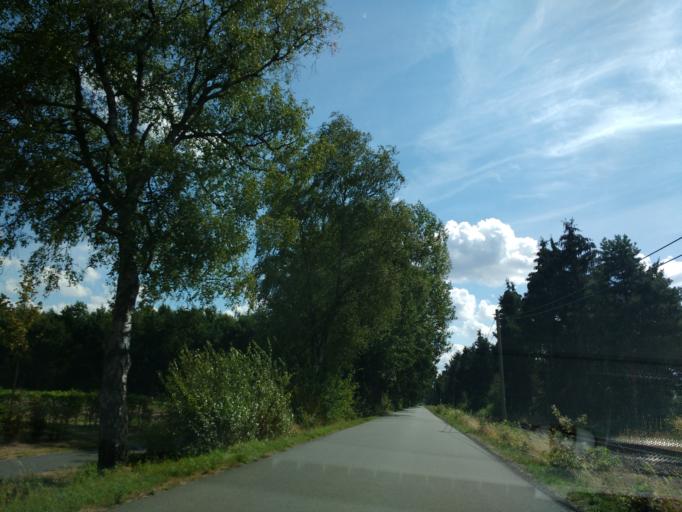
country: DE
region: North Rhine-Westphalia
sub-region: Regierungsbezirk Detmold
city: Hovelhof
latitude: 51.8002
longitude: 8.6859
